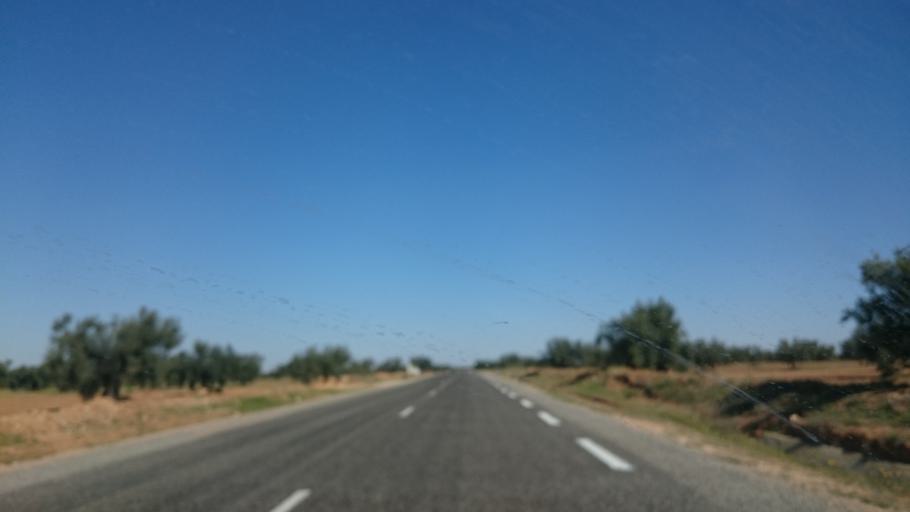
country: TN
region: Safaqis
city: Sfax
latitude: 34.8283
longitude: 10.4669
